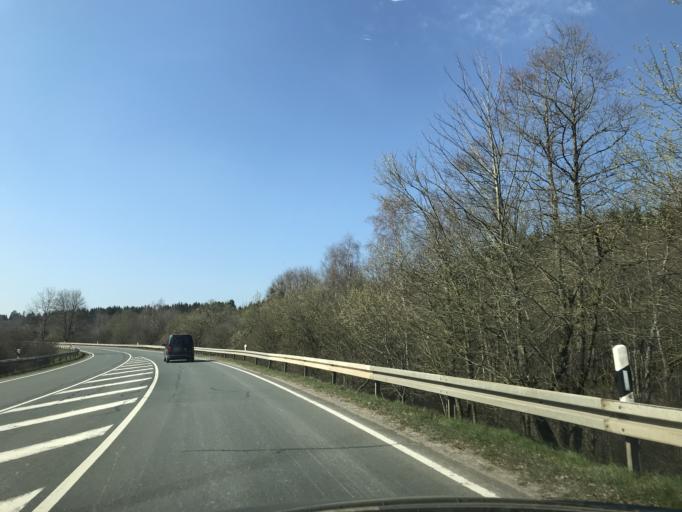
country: DE
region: Rheinland-Pfalz
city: Neuhutten
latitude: 49.6051
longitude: 7.0424
